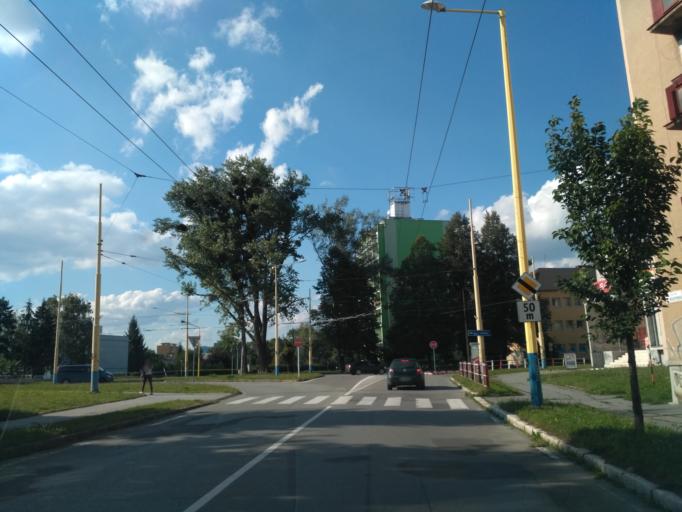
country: SK
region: Presovsky
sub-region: Okres Presov
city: Presov
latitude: 48.9942
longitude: 21.2322
